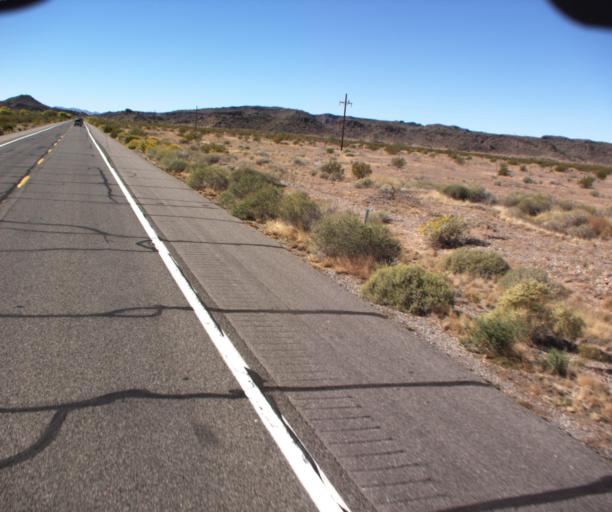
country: US
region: Arizona
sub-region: Pima County
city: Ajo
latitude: 32.5782
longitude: -112.8743
